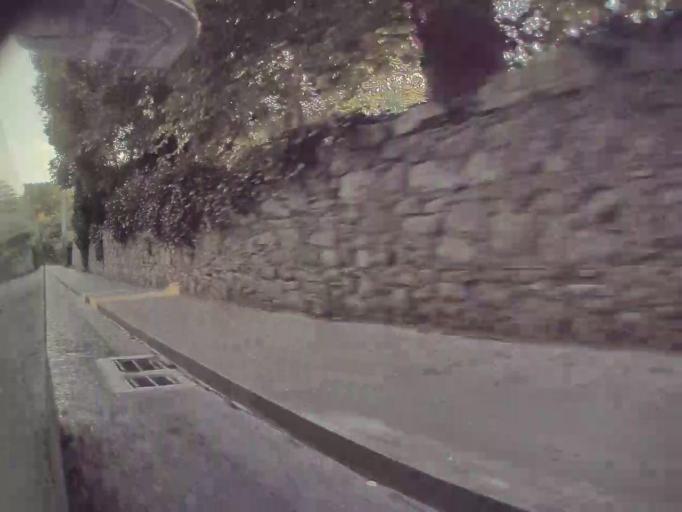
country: IE
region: Leinster
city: Sandyford
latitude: 53.2576
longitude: -6.2143
